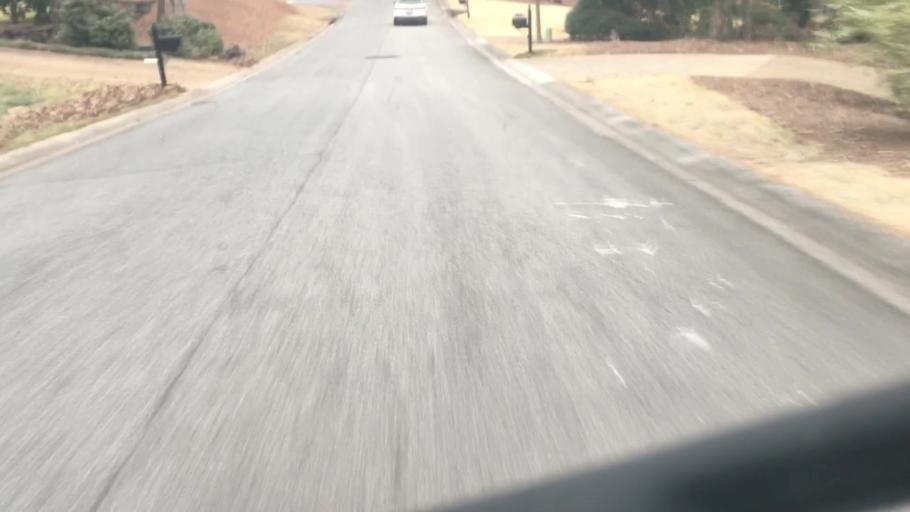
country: US
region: Alabama
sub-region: Shelby County
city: Helena
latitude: 33.3473
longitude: -86.8237
